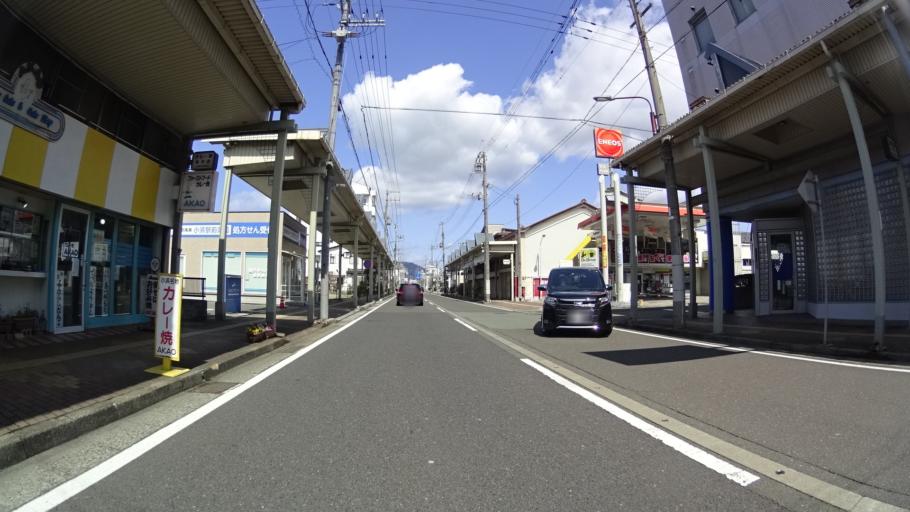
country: JP
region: Fukui
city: Obama
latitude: 35.4928
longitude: 135.7456
